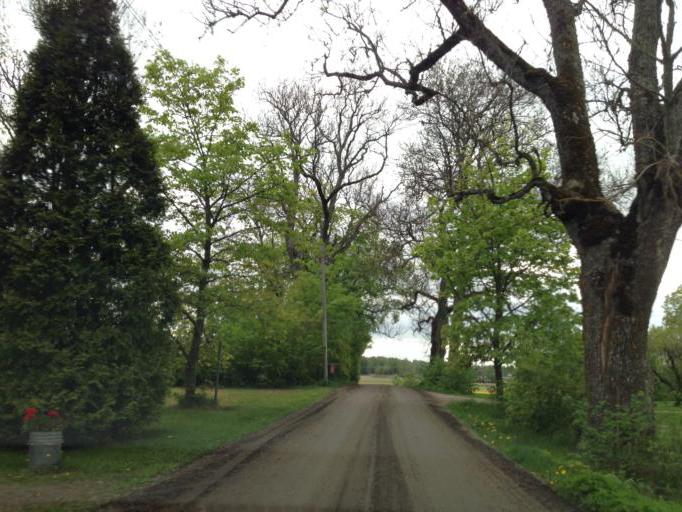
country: SE
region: Soedermanland
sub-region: Eskilstuna Kommun
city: Kvicksund
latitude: 59.4343
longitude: 16.3273
